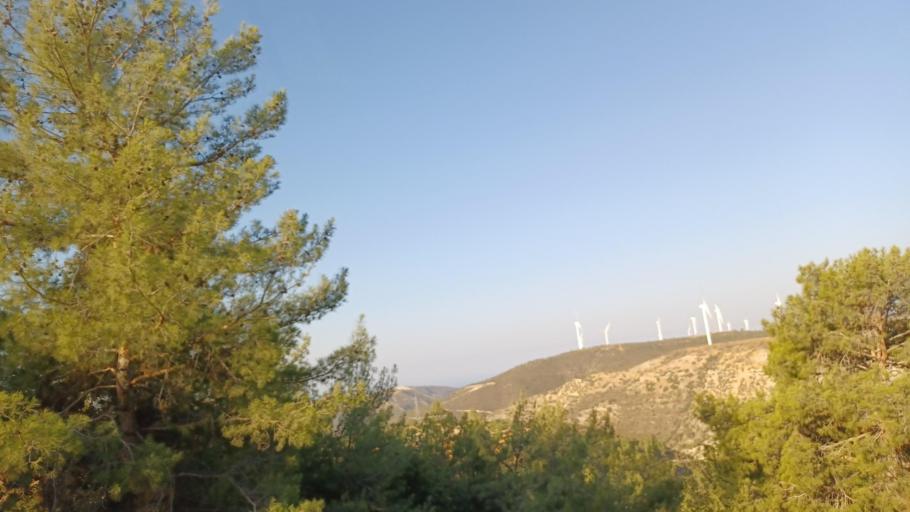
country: CY
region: Limassol
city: Pissouri
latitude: 34.7276
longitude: 32.6675
